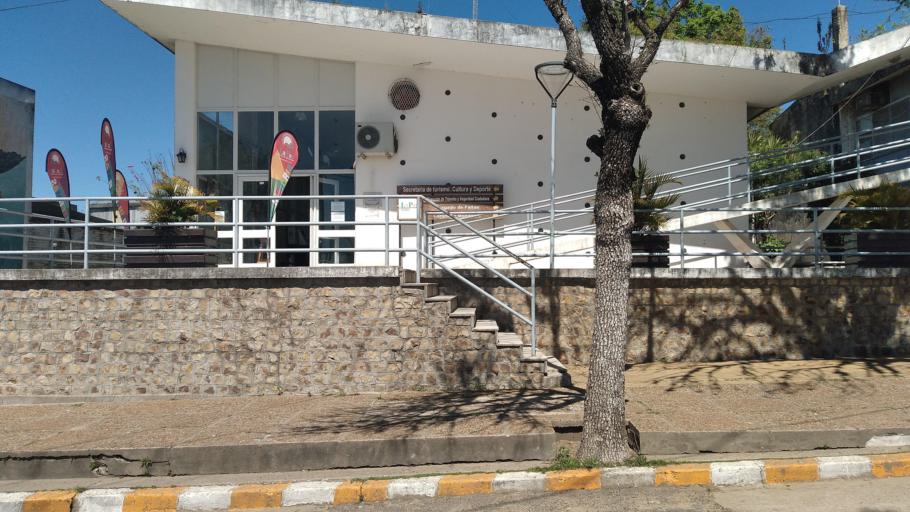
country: AR
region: Entre Rios
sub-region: Departamento de La Paz
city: La Paz
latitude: -30.7349
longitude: -59.6412
